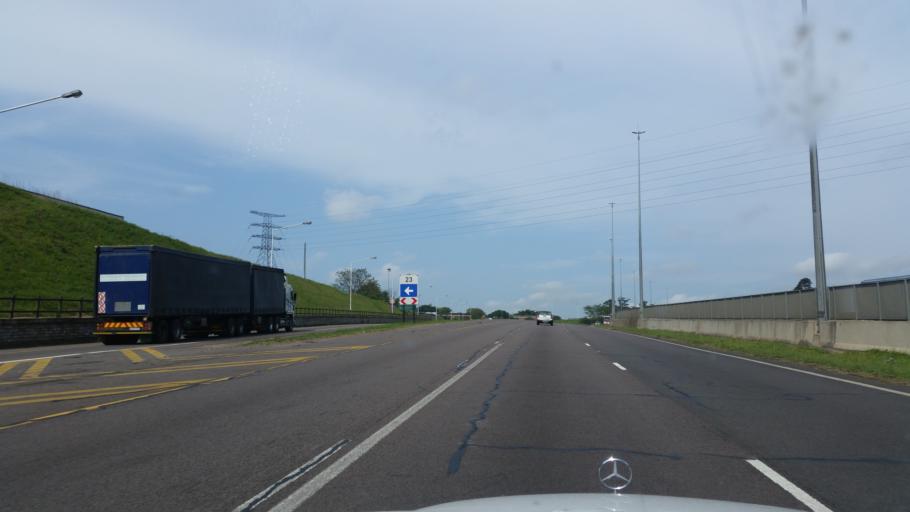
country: ZA
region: KwaZulu-Natal
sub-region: eThekwini Metropolitan Municipality
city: Berea
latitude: -29.8272
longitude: 30.8295
